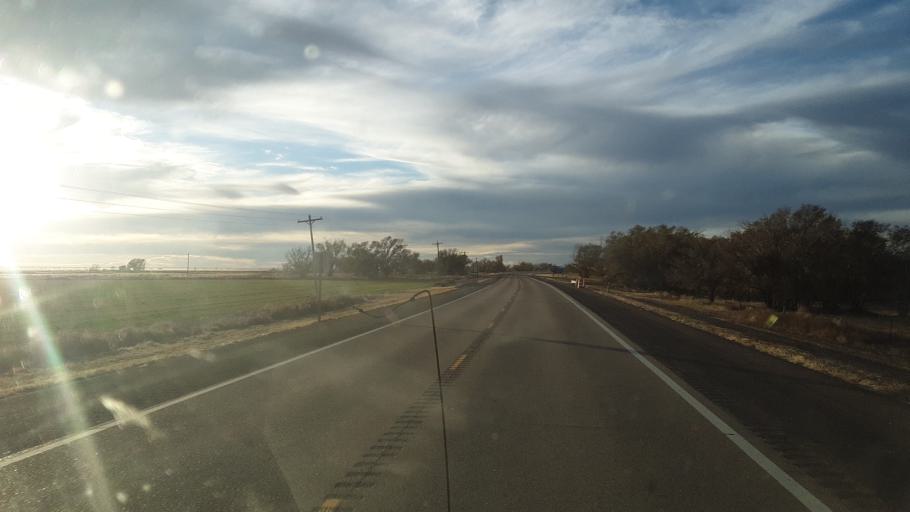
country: US
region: Kansas
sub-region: Hamilton County
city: Syracuse
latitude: 38.0475
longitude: -102.0413
